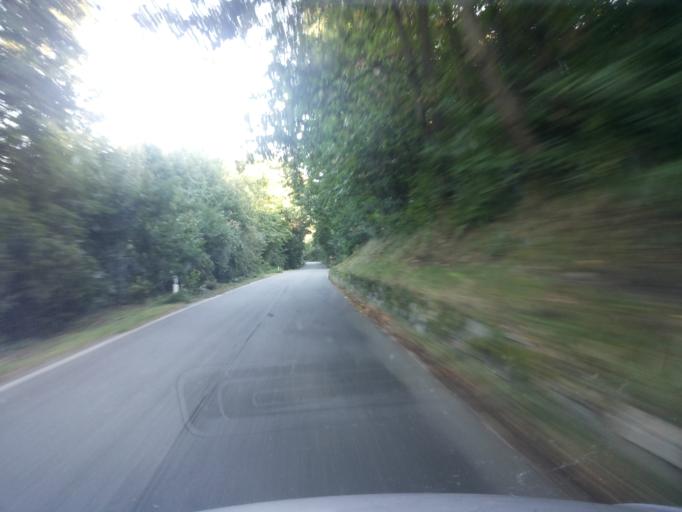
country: IT
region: Piedmont
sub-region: Provincia di Torino
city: Cossano Canavese
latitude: 45.3879
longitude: 7.9812
